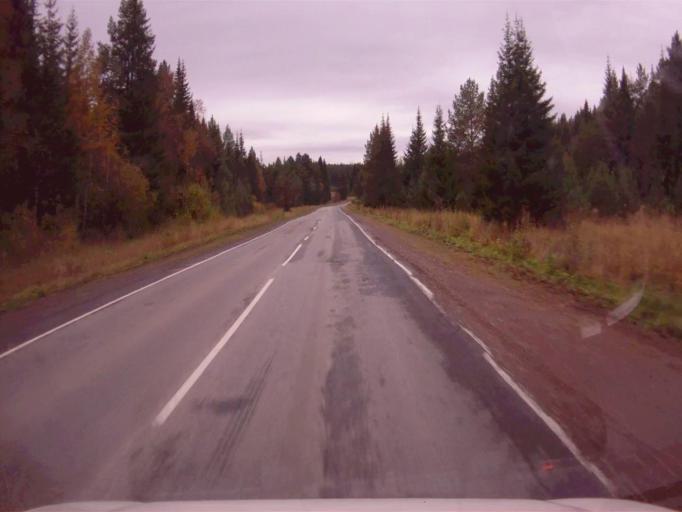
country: RU
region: Chelyabinsk
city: Nyazepetrovsk
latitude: 56.0658
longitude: 59.6640
